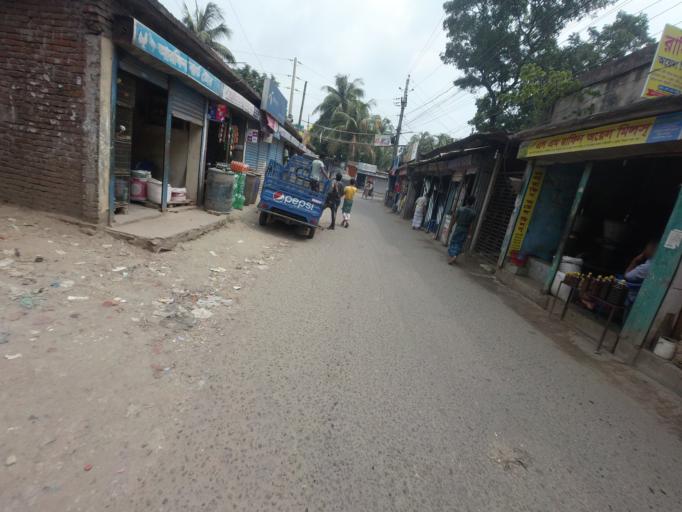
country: BD
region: Dhaka
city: Azimpur
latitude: 23.7316
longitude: 90.3341
